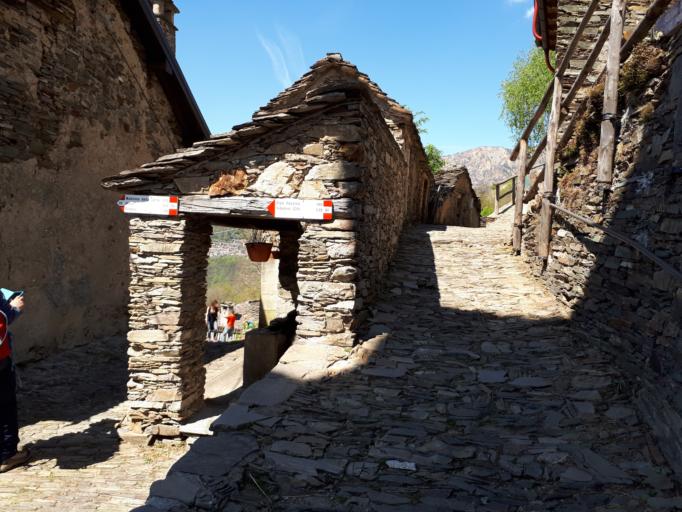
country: IT
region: Lombardy
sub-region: Provincia di Varese
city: Curiglia
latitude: 46.0710
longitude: 8.8271
